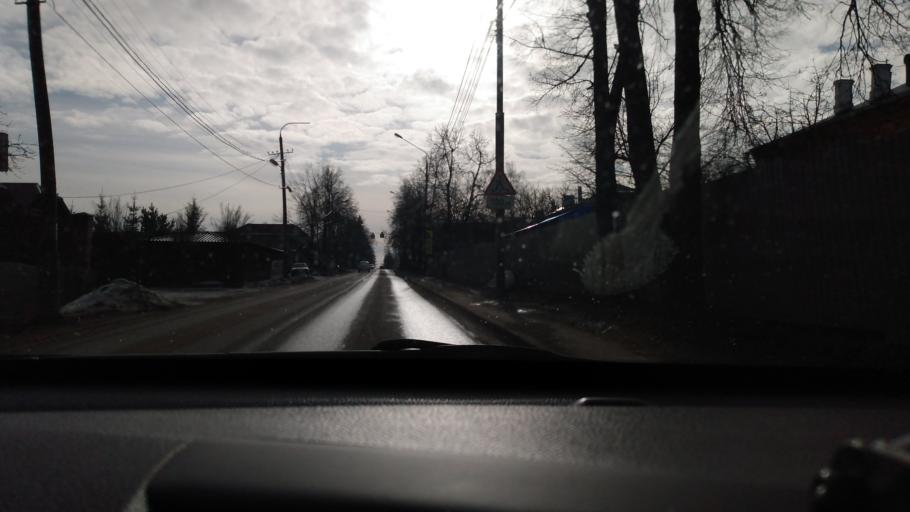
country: RU
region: Moskovskaya
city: Nakhabino
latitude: 55.8656
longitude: 37.1849
